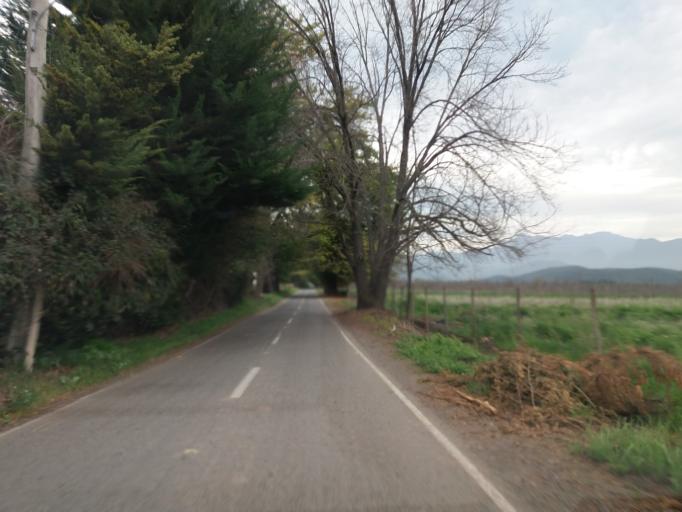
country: CL
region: Valparaiso
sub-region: Provincia de Quillota
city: Quillota
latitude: -32.8980
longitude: -71.1062
